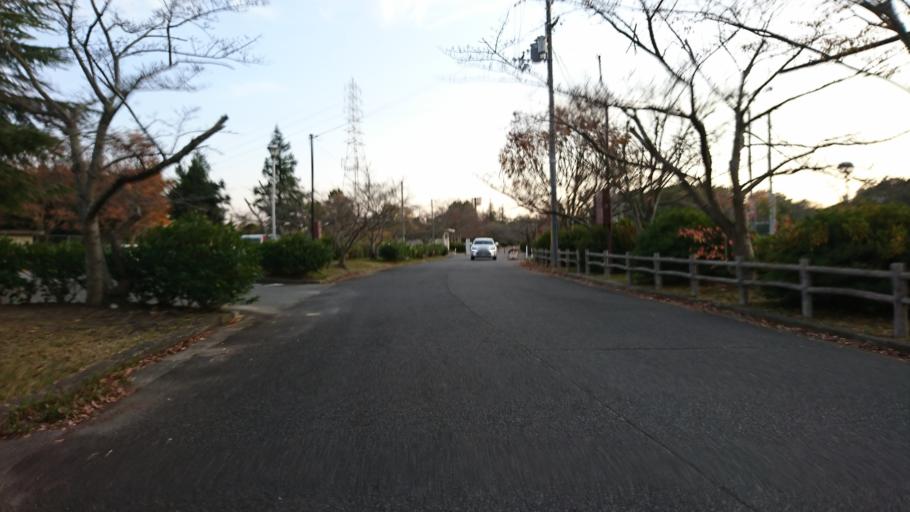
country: JP
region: Hyogo
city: Kakogawacho-honmachi
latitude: 34.7819
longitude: 134.8651
